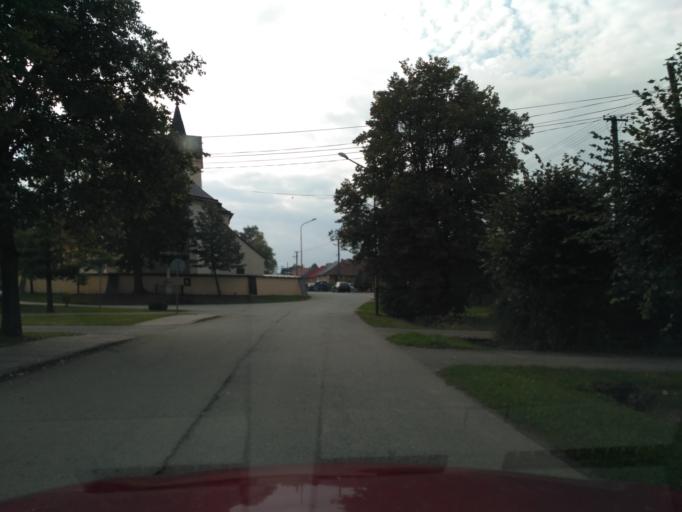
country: SK
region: Kosicky
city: Kosice
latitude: 48.6370
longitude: 21.1702
